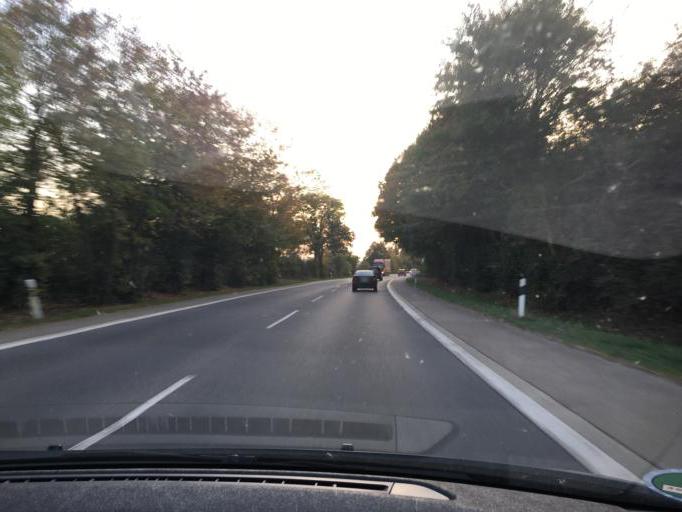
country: DE
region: North Rhine-Westphalia
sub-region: Regierungsbezirk Koln
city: Erftstadt
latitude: 50.8429
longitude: 6.7822
